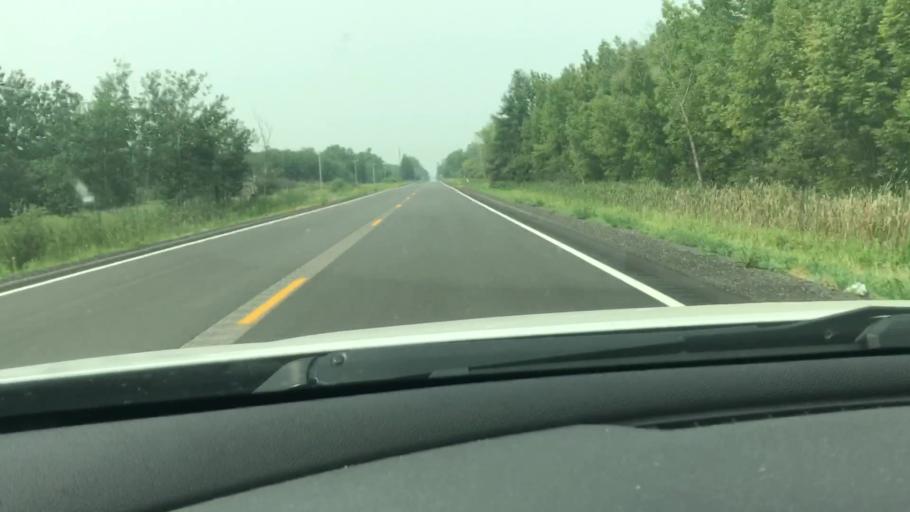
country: US
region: Minnesota
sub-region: Itasca County
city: Cohasset
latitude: 47.3632
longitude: -93.8694
